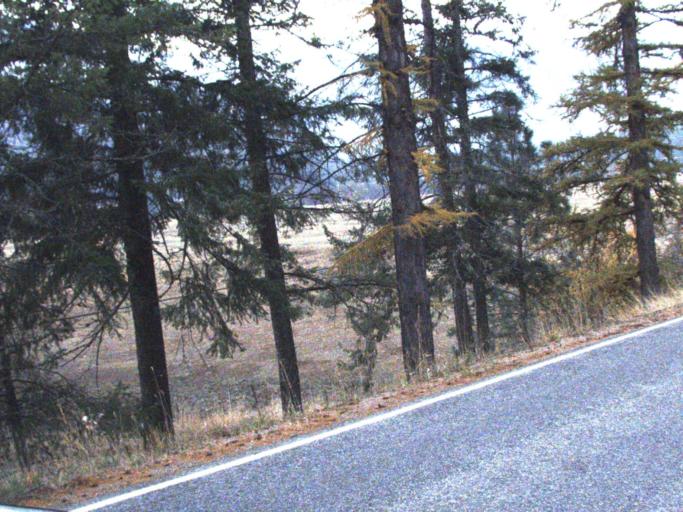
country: CA
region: British Columbia
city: Grand Forks
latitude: 48.9767
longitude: -118.2238
